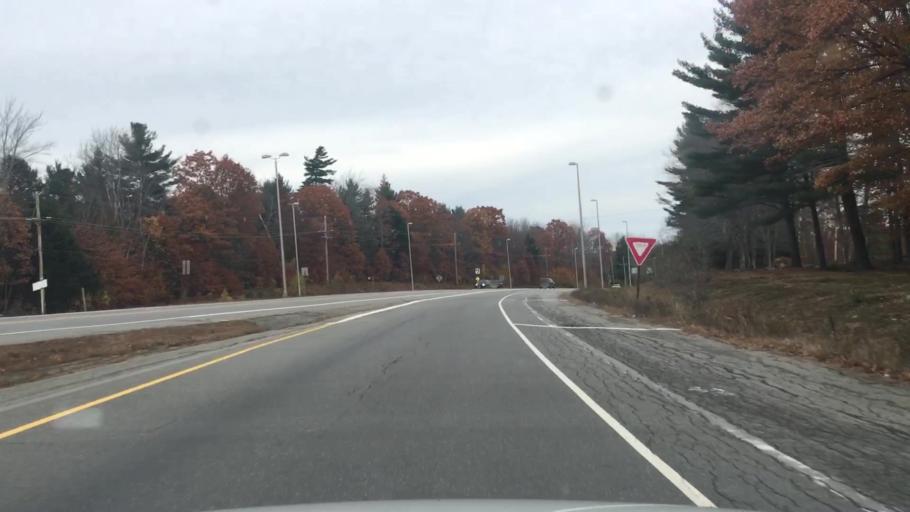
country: US
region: Maine
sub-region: Waldo County
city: Belfast
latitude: 44.4267
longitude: -69.0217
